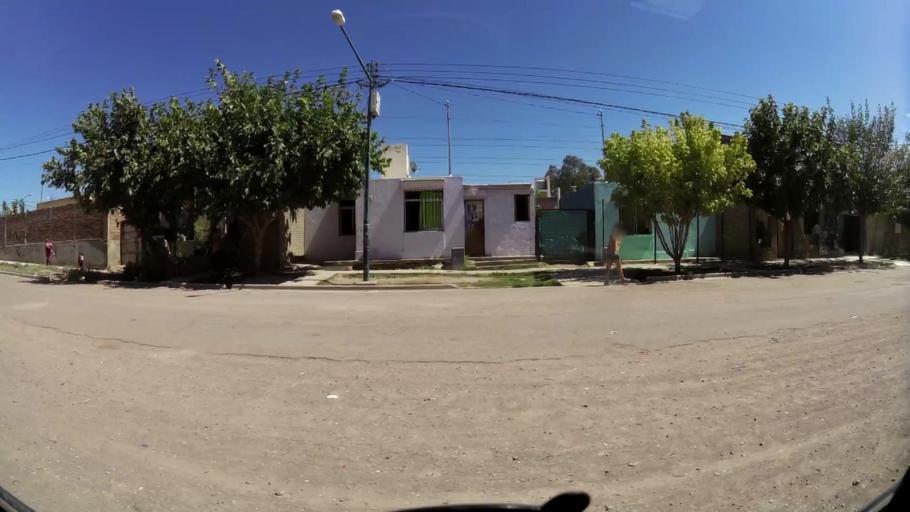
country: AR
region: Mendoza
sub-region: Departamento de Godoy Cruz
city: Godoy Cruz
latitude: -32.9302
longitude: -68.8679
